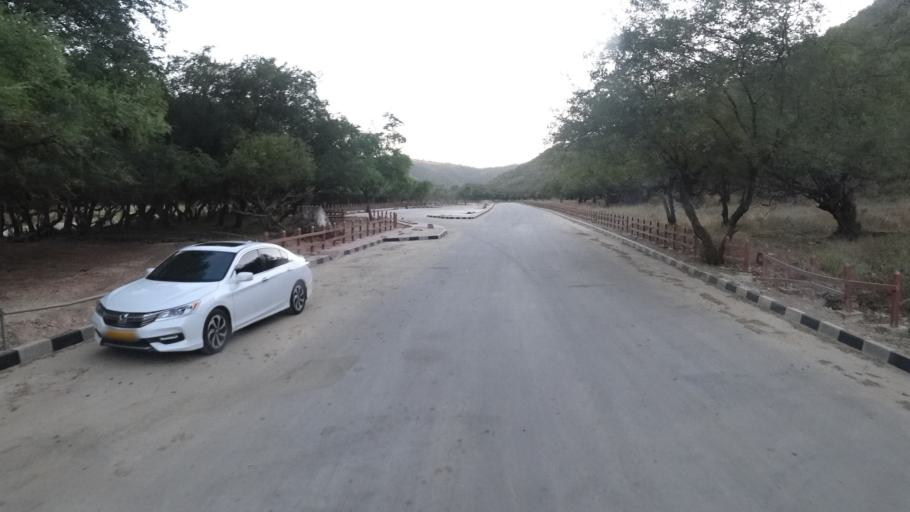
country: OM
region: Zufar
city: Salalah
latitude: 17.1033
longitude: 54.4522
